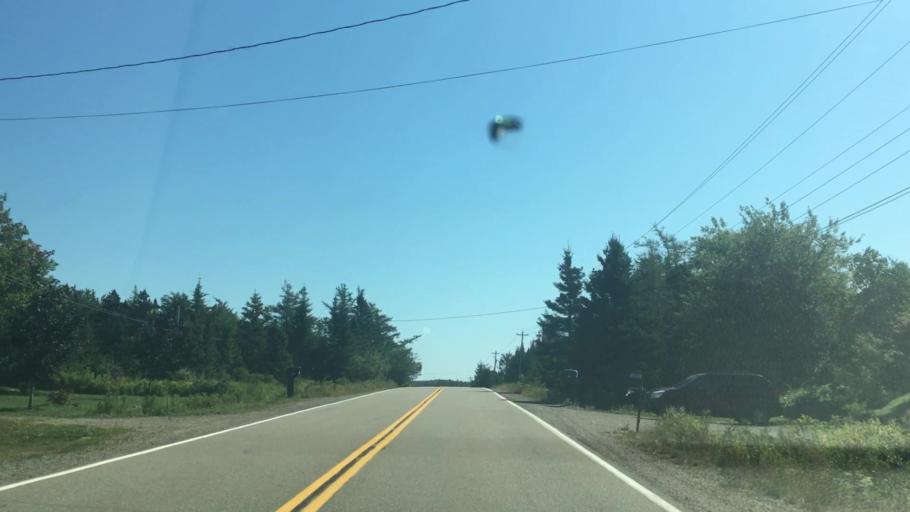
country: CA
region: Nova Scotia
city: Antigonish
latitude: 45.0242
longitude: -62.0234
